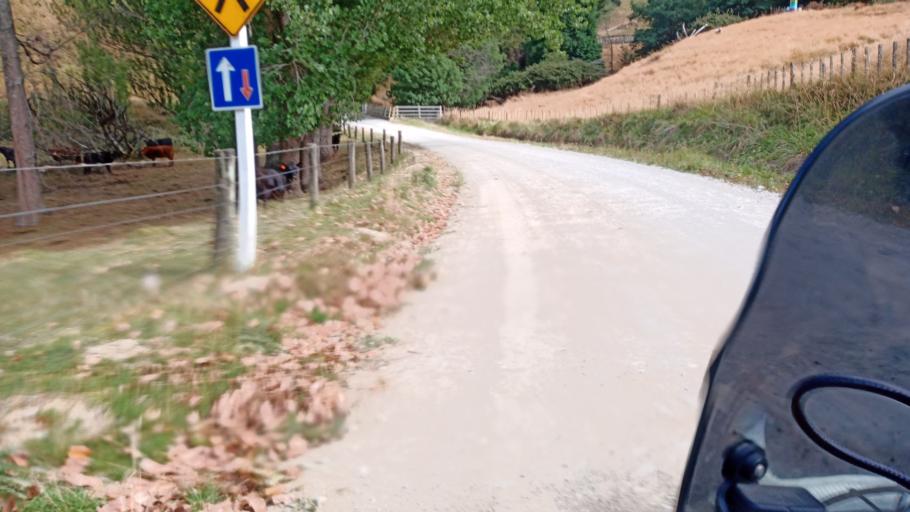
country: NZ
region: Hawke's Bay
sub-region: Wairoa District
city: Wairoa
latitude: -38.6035
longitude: 177.4876
